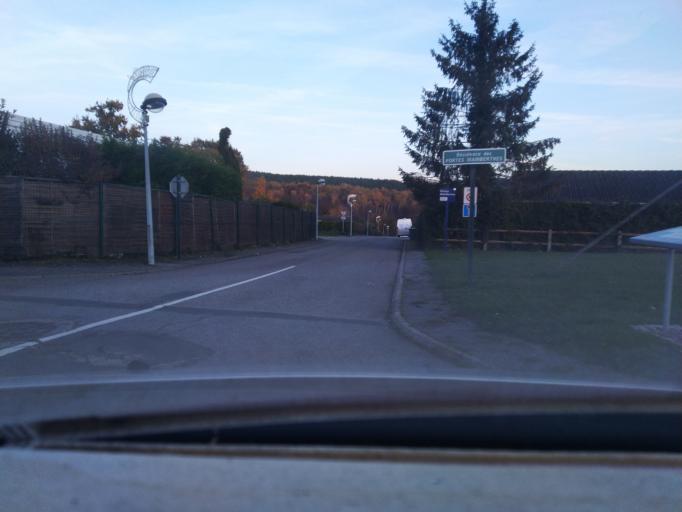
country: FR
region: Haute-Normandie
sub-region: Departement de la Seine-Maritime
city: Yainville
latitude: 49.4480
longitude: 0.8285
